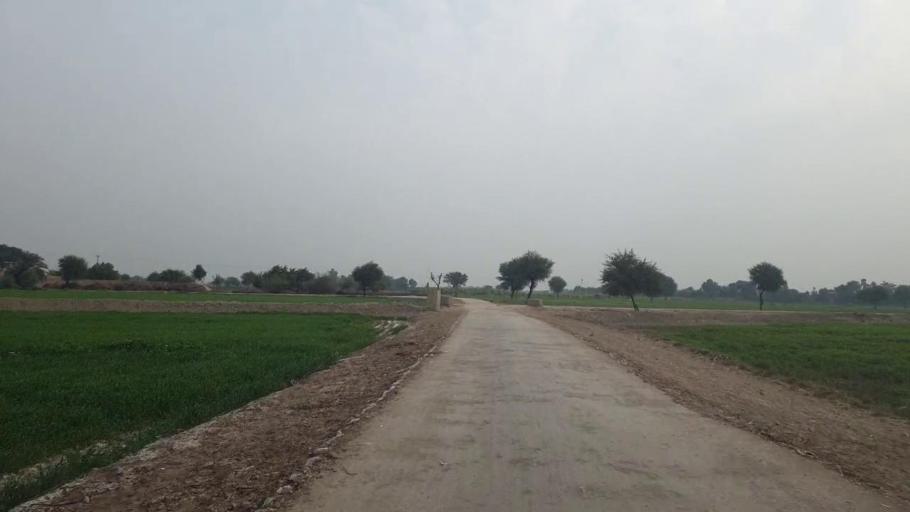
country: PK
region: Sindh
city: Shahdadpur
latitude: 25.9497
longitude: 68.7026
